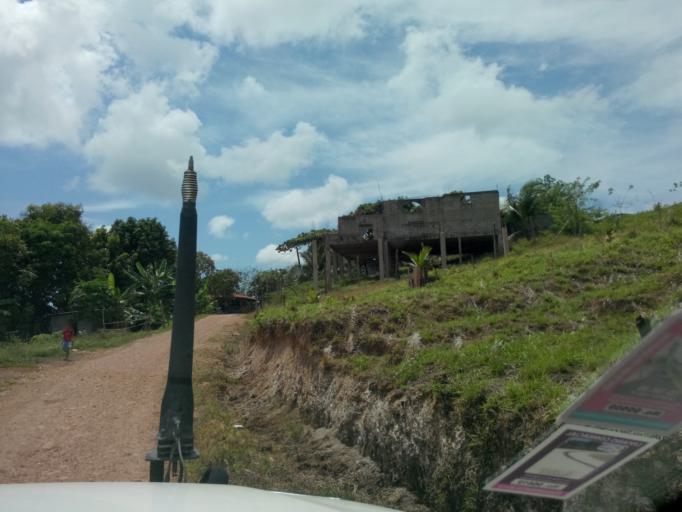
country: NI
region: Atlantico Sur
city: Bluefields
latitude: 12.0092
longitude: -83.7741
